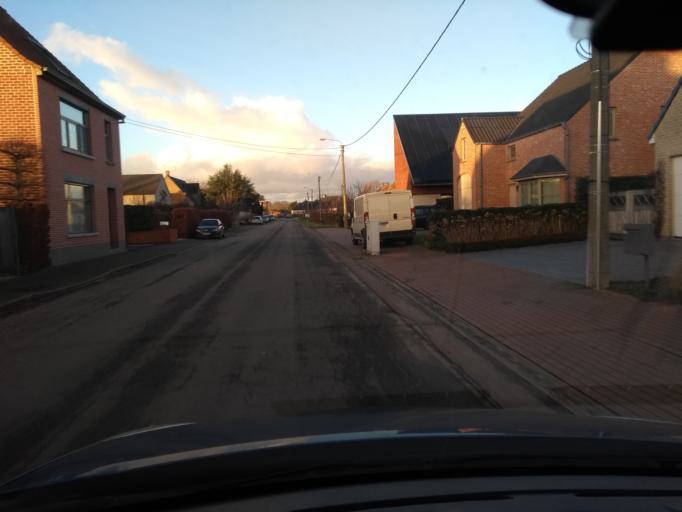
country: BE
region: Flanders
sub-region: Provincie West-Vlaanderen
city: Ruiselede
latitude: 51.0750
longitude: 3.3538
